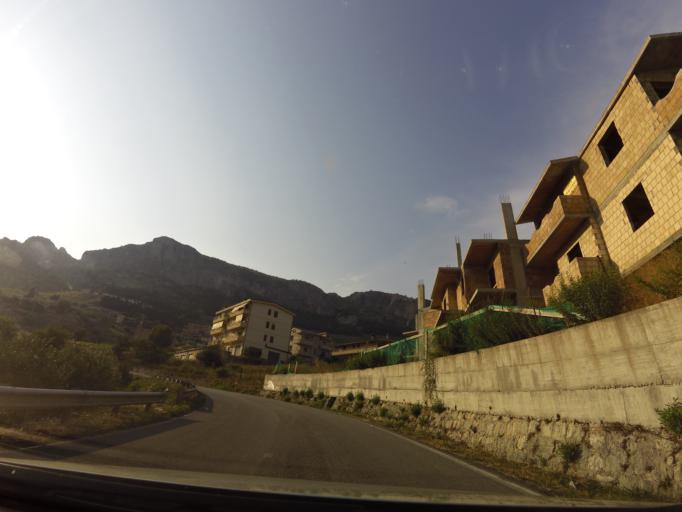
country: IT
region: Calabria
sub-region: Provincia di Reggio Calabria
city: Stilo
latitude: 38.4714
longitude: 16.4670
